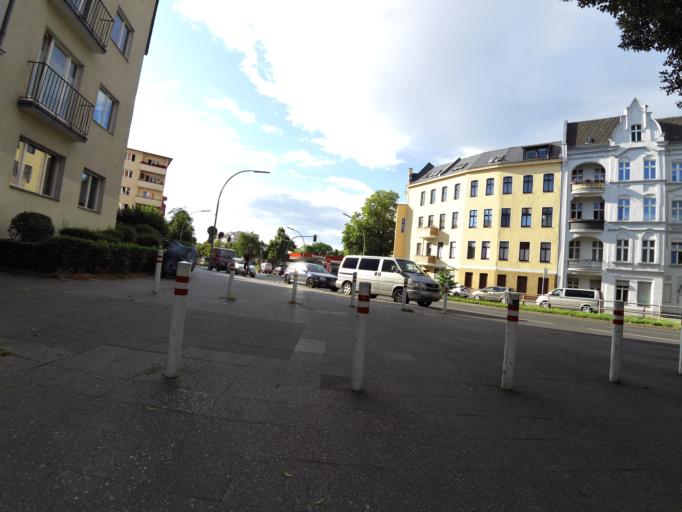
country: DE
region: Berlin
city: Steglitz Bezirk
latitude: 52.4510
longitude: 13.3360
